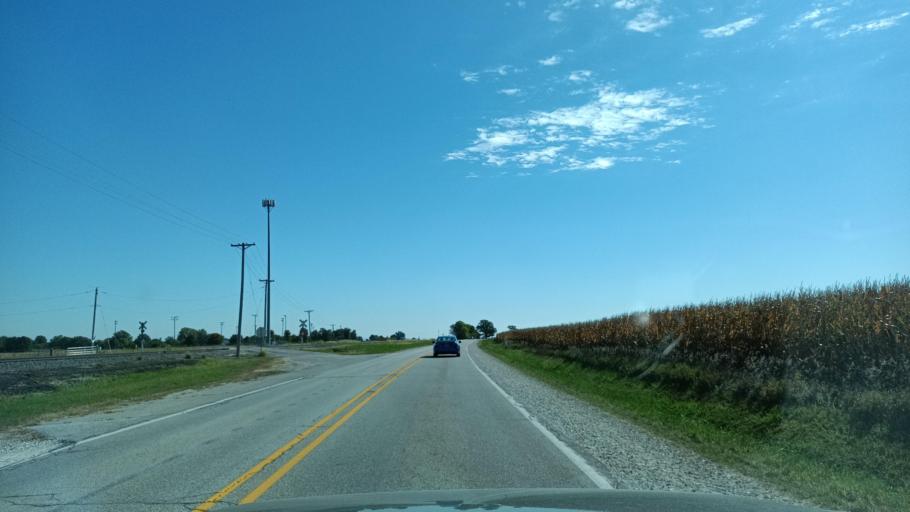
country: US
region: Illinois
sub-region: Knox County
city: Knoxville
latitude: 40.9078
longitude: -90.2592
